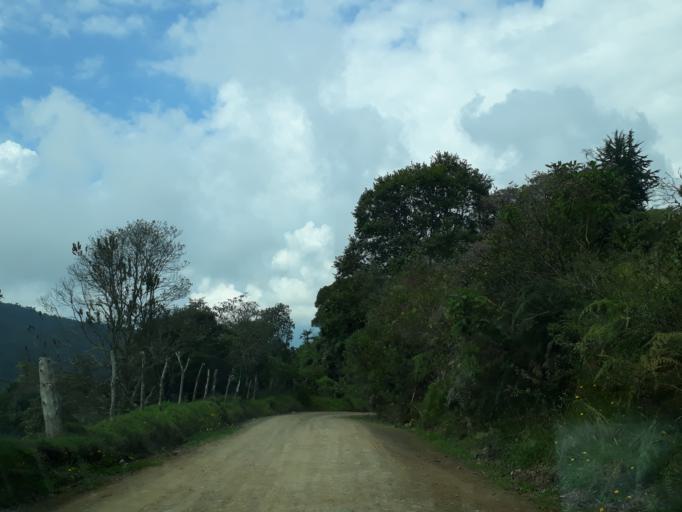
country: CO
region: Cundinamarca
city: Macheta
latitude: 5.1091
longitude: -73.5404
